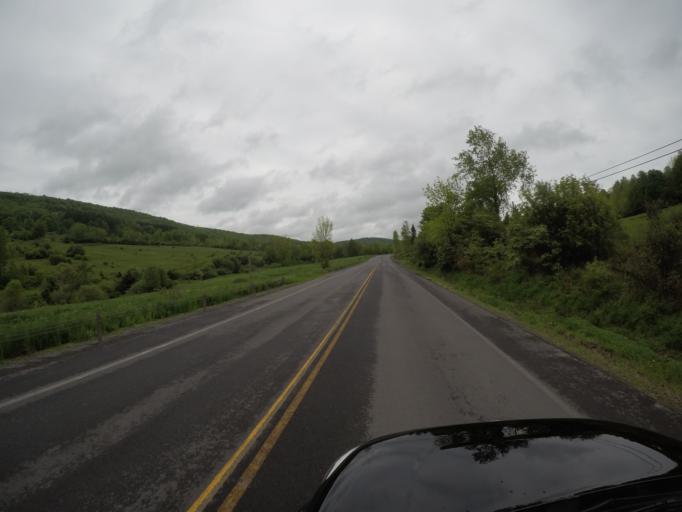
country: US
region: New York
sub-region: Delaware County
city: Delhi
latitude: 42.2034
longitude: -74.7927
